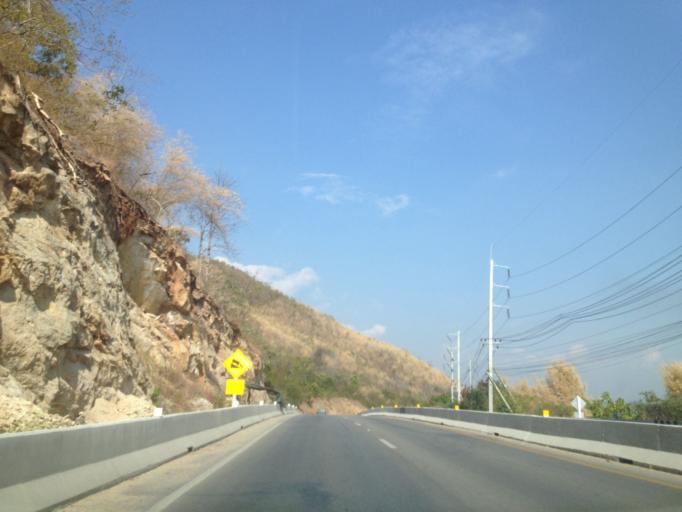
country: TH
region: Chiang Mai
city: Chom Thong
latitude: 18.3751
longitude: 98.6791
